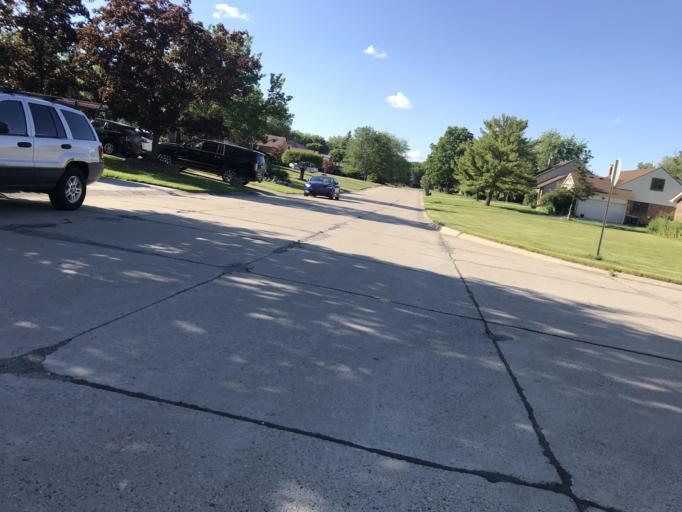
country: US
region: Michigan
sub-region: Oakland County
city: Farmington
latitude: 42.4717
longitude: -83.3467
